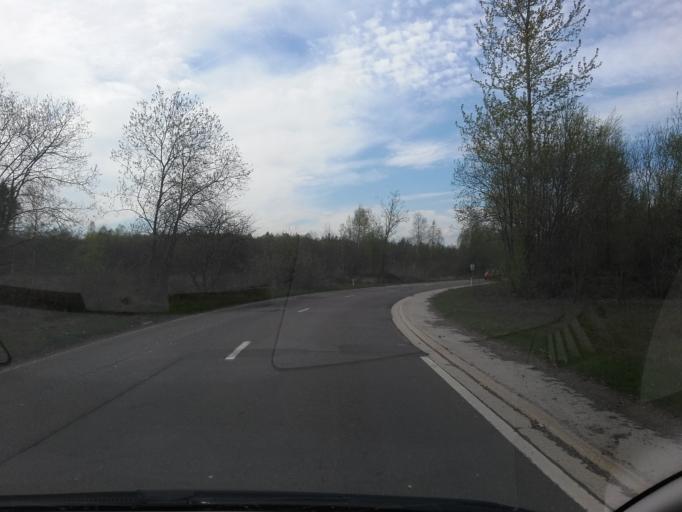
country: BE
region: Wallonia
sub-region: Province du Luxembourg
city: Etalle
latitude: 49.6655
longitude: 5.5935
